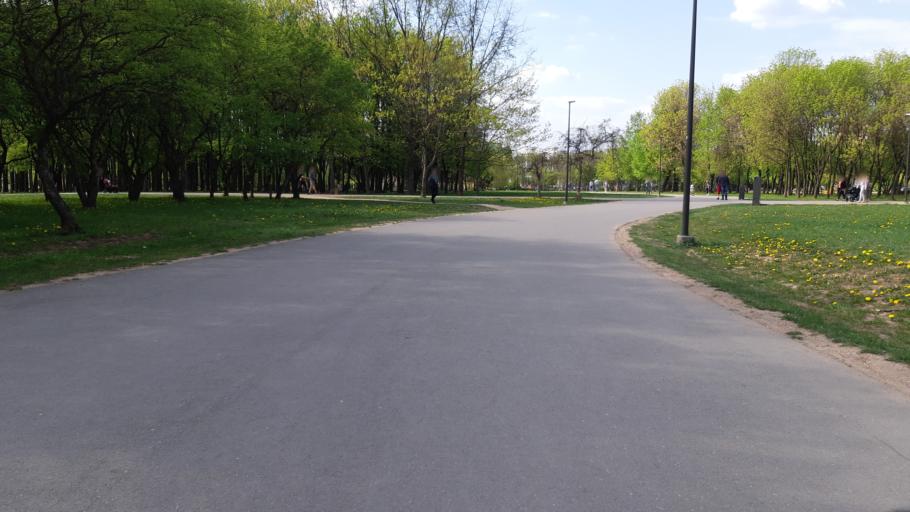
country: LT
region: Kauno apskritis
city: Dainava (Kaunas)
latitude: 54.9227
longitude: 23.9521
